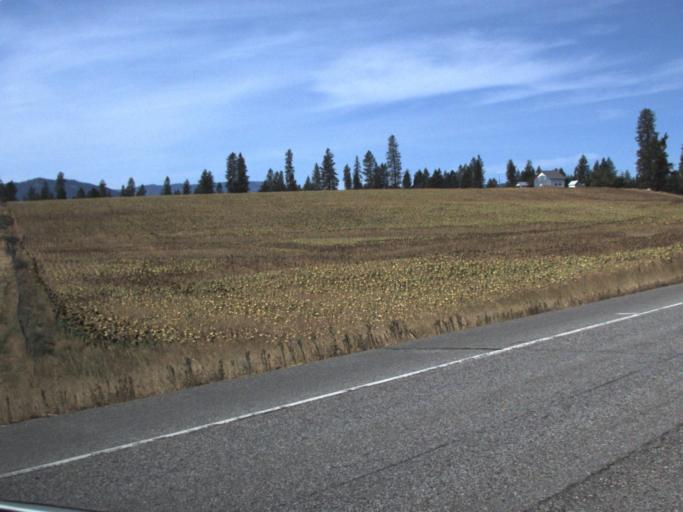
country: US
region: Washington
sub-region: Stevens County
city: Chewelah
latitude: 48.1648
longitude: -117.6977
